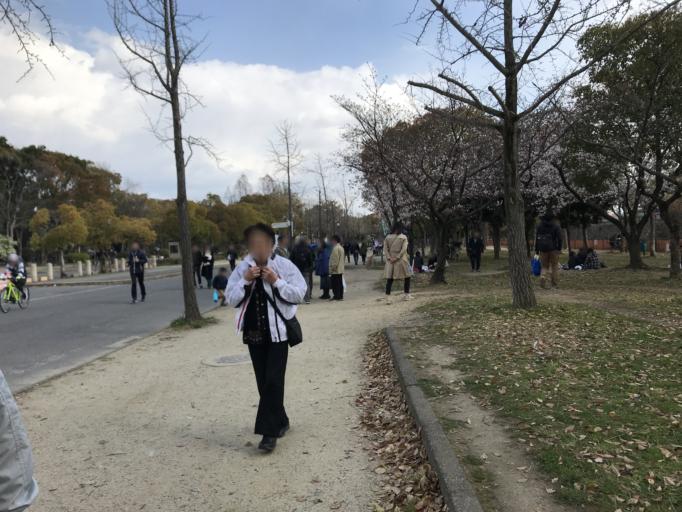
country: JP
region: Osaka
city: Osaka-shi
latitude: 34.6905
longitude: 135.5271
